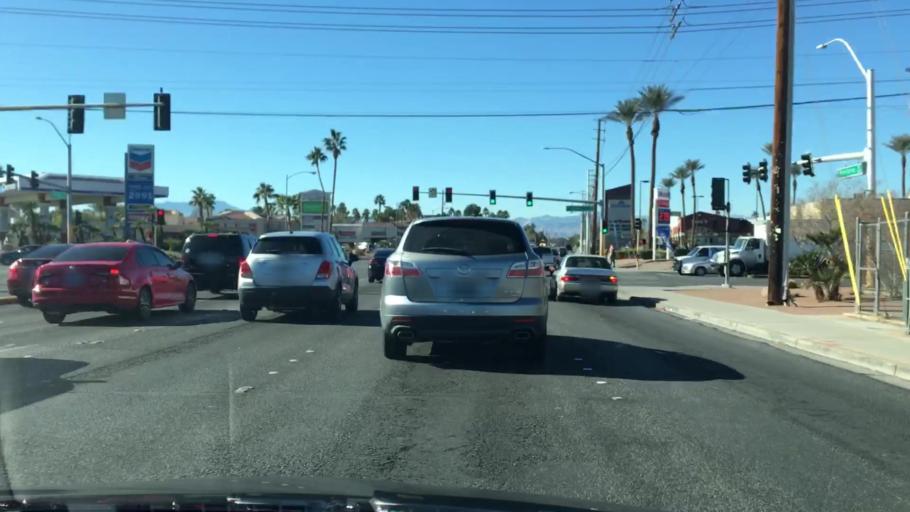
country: US
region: Nevada
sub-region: Clark County
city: Whitney
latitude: 36.0570
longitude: -115.1178
